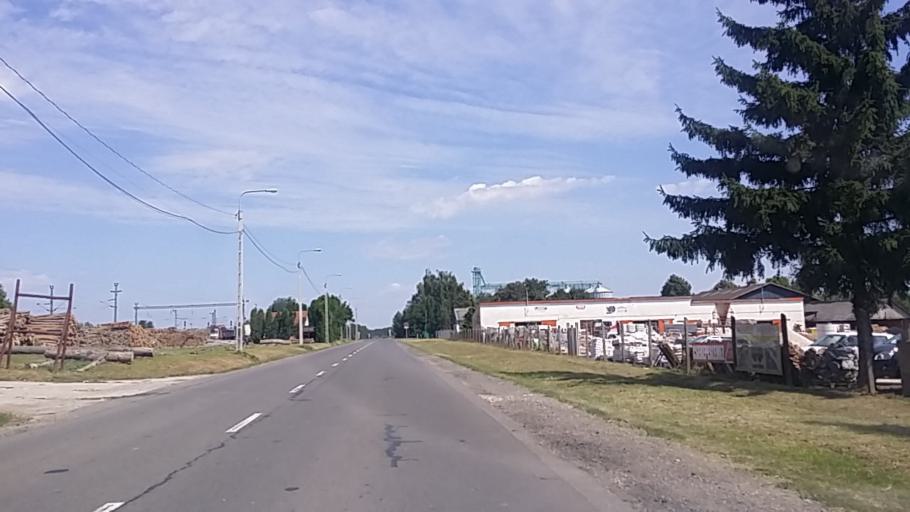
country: HU
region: Baranya
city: Sasd
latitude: 46.2603
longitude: 18.1056
